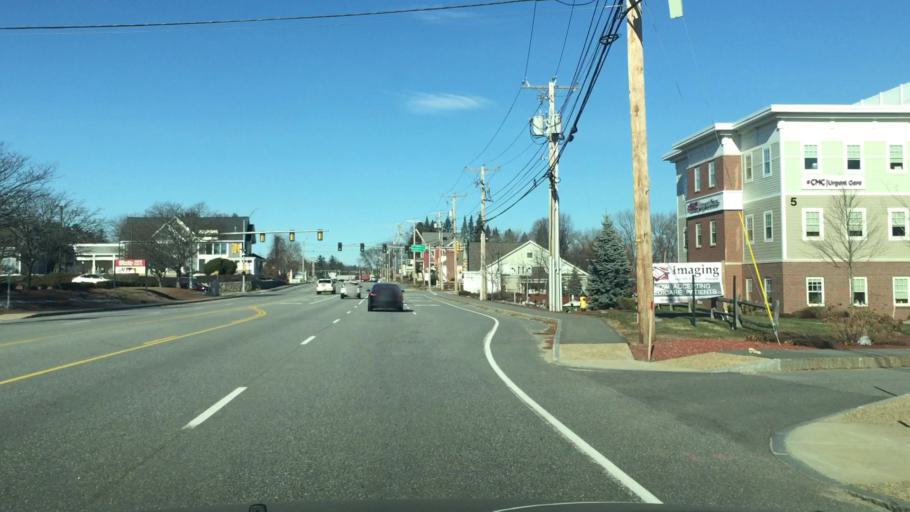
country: US
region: New Hampshire
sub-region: Hillsborough County
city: Bedford
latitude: 42.9601
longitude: -71.4794
